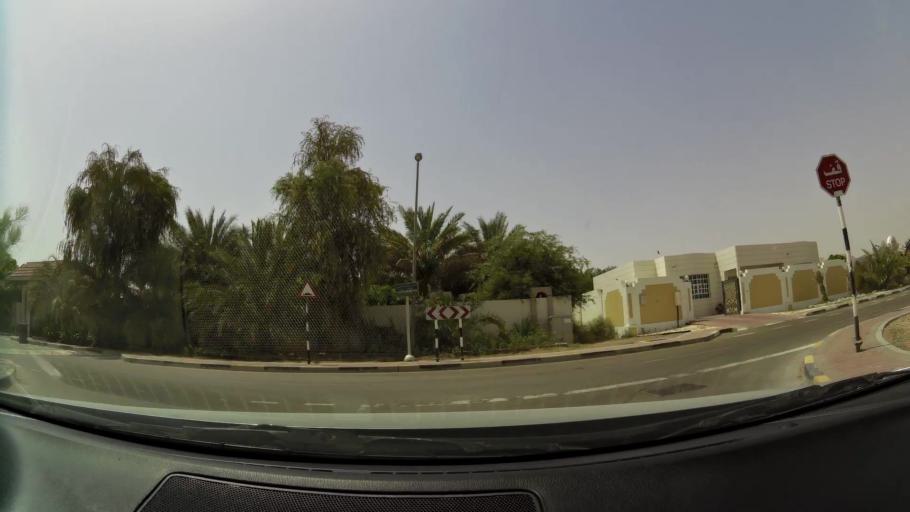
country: AE
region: Abu Dhabi
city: Al Ain
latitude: 24.1758
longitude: 55.7094
